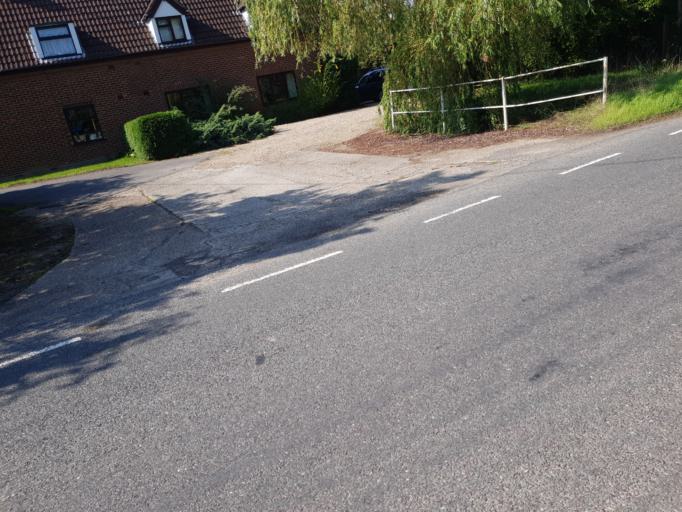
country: GB
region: England
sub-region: Suffolk
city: East Bergholt
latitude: 51.9347
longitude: 0.9929
